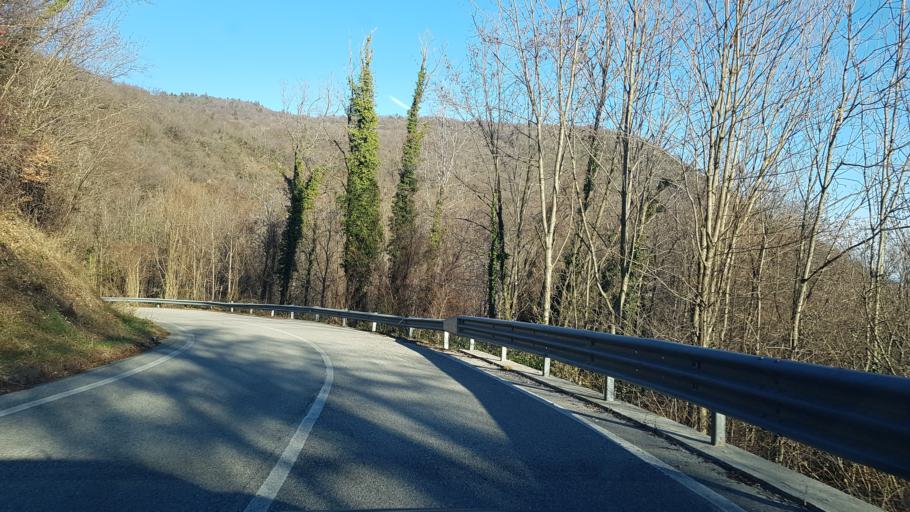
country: IT
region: Friuli Venezia Giulia
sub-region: Provincia di Udine
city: Forgaria nel Friuli
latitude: 46.2286
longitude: 12.9941
